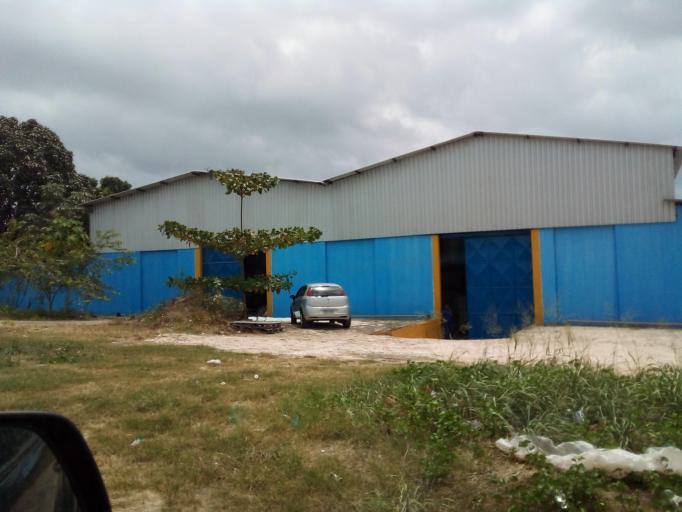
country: BR
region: Maranhao
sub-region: Sao Luis
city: Sao Luis
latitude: -2.6910
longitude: -44.3031
